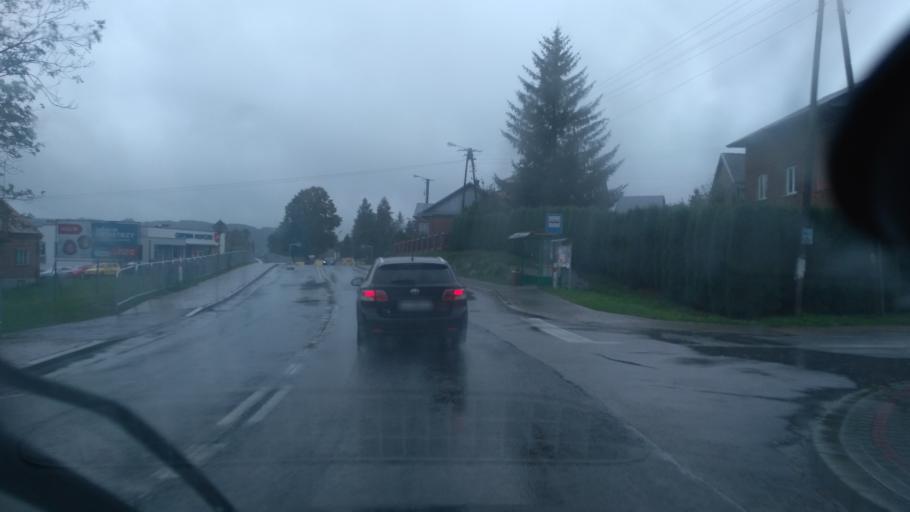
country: PL
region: Subcarpathian Voivodeship
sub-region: Powiat ropczycko-sedziszowski
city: Niedzwiada
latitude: 49.9975
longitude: 21.5632
